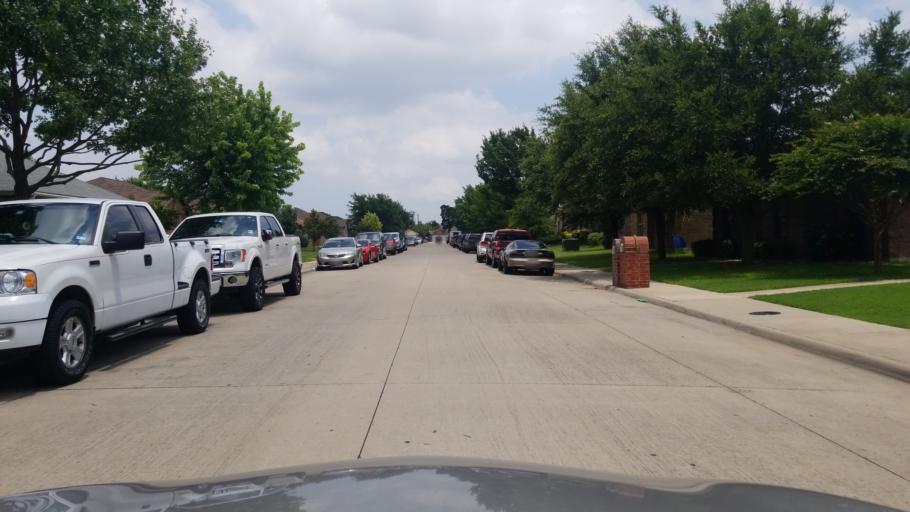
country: US
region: Texas
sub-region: Dallas County
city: Duncanville
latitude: 32.6863
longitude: -96.9152
